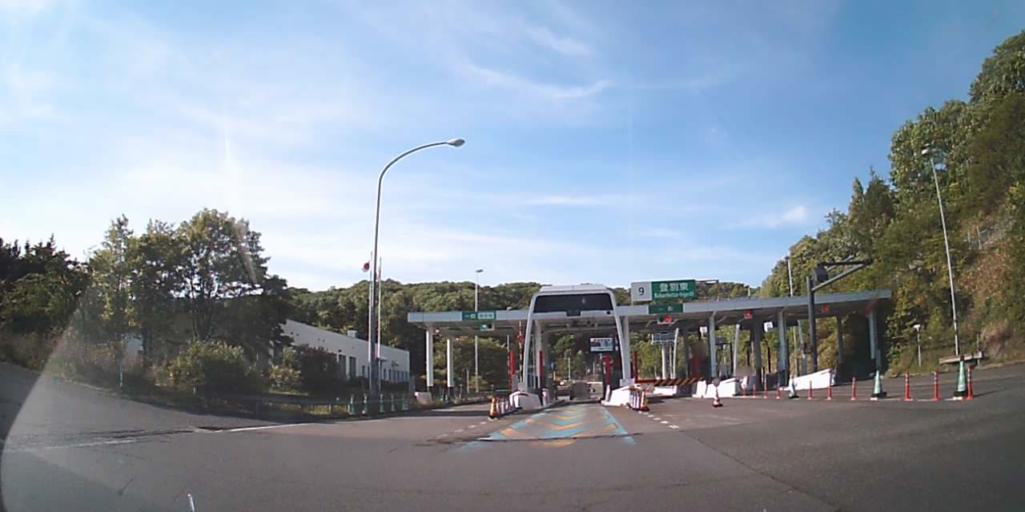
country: JP
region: Hokkaido
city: Shiraoi
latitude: 42.4635
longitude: 141.1735
